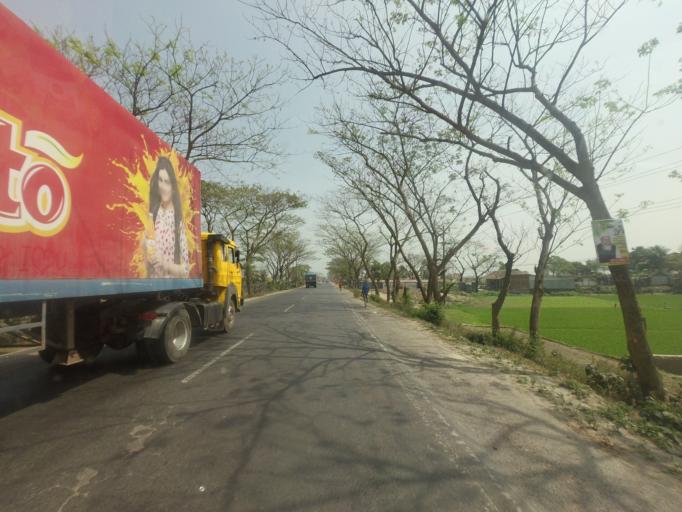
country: BD
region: Dhaka
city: Bhairab Bazar
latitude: 24.0489
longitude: 91.1023
